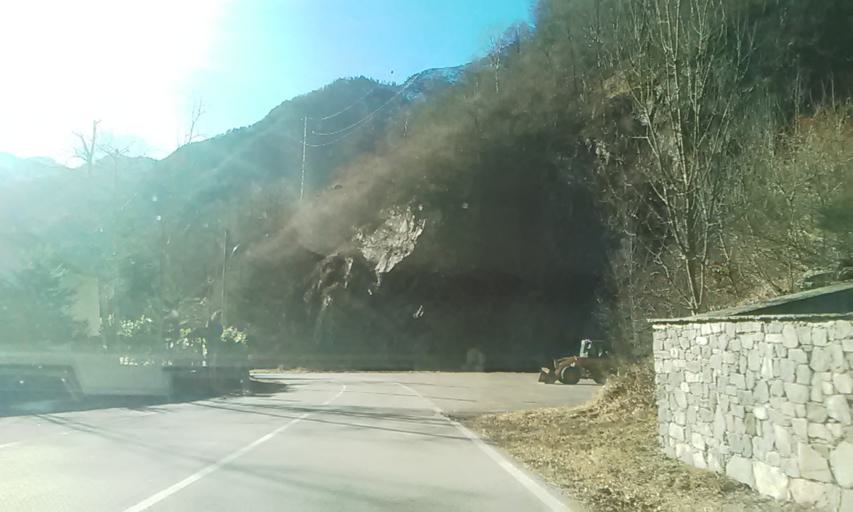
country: IT
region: Piedmont
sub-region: Provincia di Vercelli
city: Rimasco
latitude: 45.8646
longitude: 8.0654
